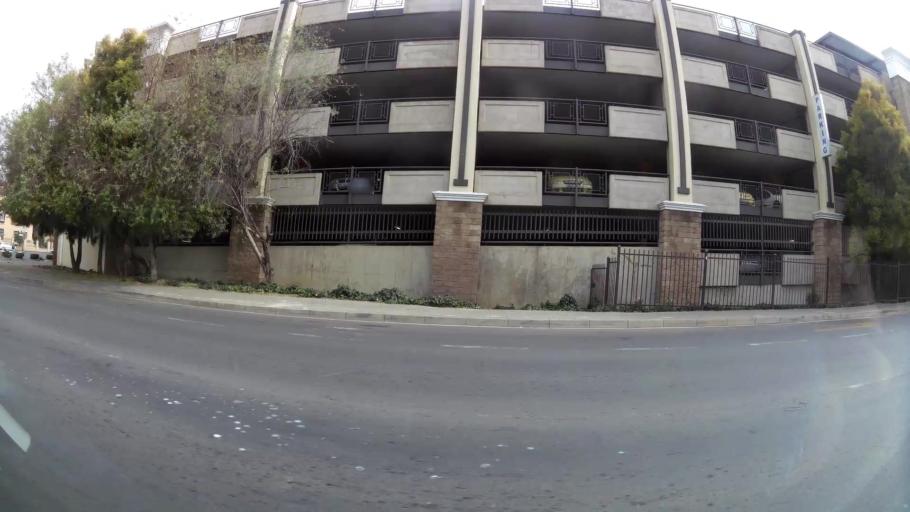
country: ZA
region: Orange Free State
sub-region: Mangaung Metropolitan Municipality
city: Bloemfontein
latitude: -29.1094
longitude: 26.2022
